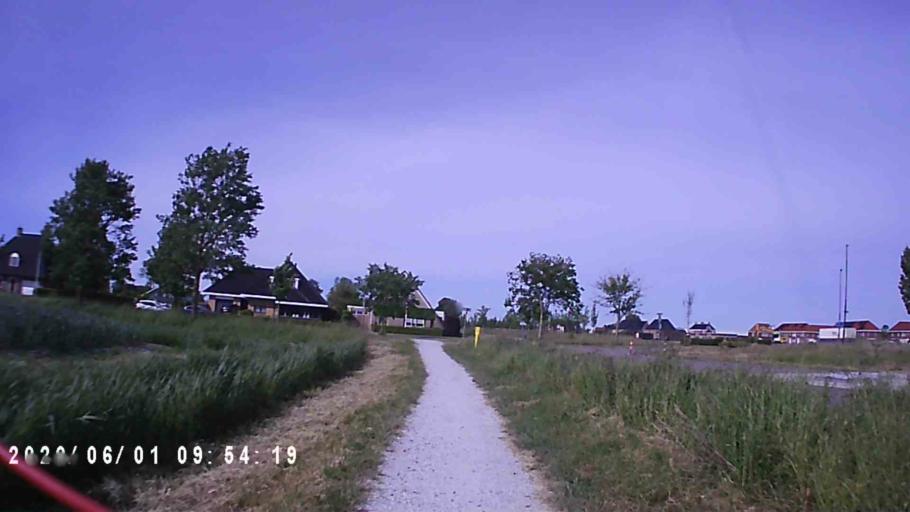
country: NL
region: Friesland
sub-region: Menameradiel
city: Berltsum
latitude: 53.2384
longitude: 5.6510
